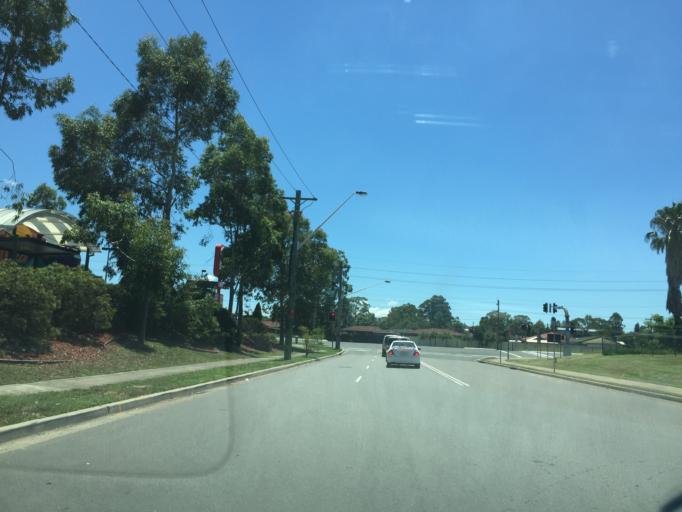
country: AU
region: New South Wales
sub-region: Blacktown
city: Mount Druitt
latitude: -33.7788
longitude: 150.8089
